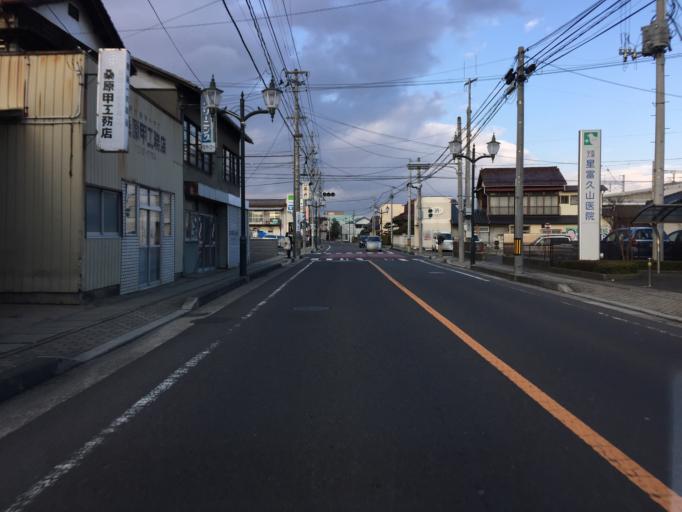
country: JP
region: Fukushima
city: Koriyama
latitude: 37.4100
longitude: 140.3906
